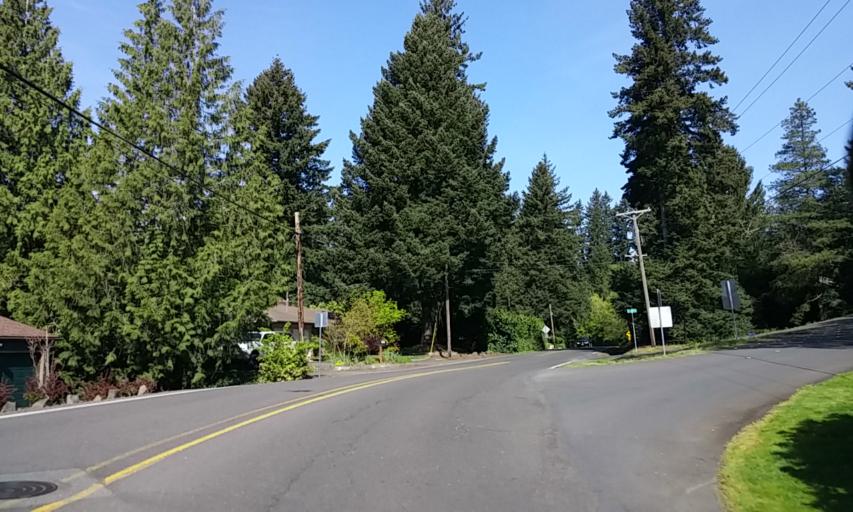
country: US
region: Oregon
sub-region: Washington County
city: Cedar Hills
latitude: 45.4969
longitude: -122.7859
